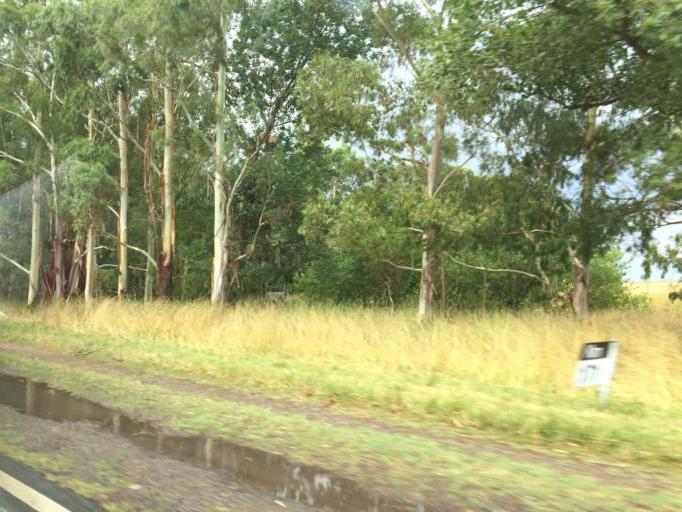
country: AR
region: Buenos Aires
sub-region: Partido de Rauch
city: Rauch
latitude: -36.9740
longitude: -58.9966
